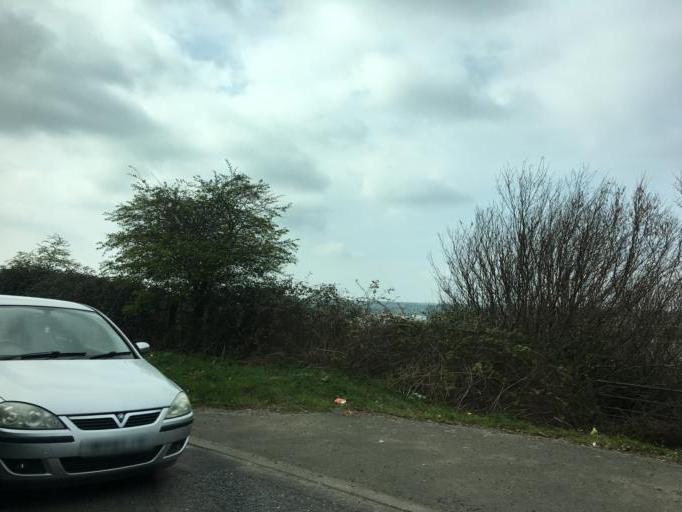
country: GB
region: Wales
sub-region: Gwynedd
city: Caernarfon
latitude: 53.1605
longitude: -4.2503
